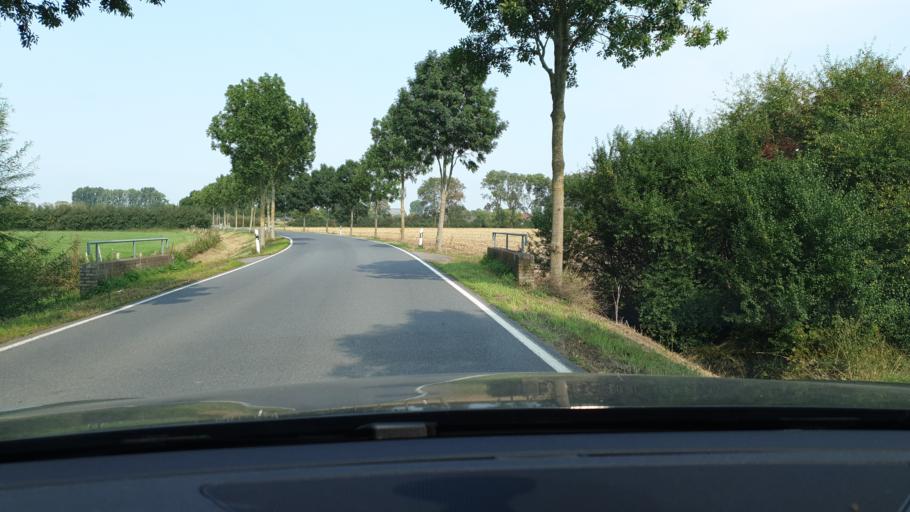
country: DE
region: North Rhine-Westphalia
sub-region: Regierungsbezirk Dusseldorf
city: Kranenburg
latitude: 51.8198
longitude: 6.0179
